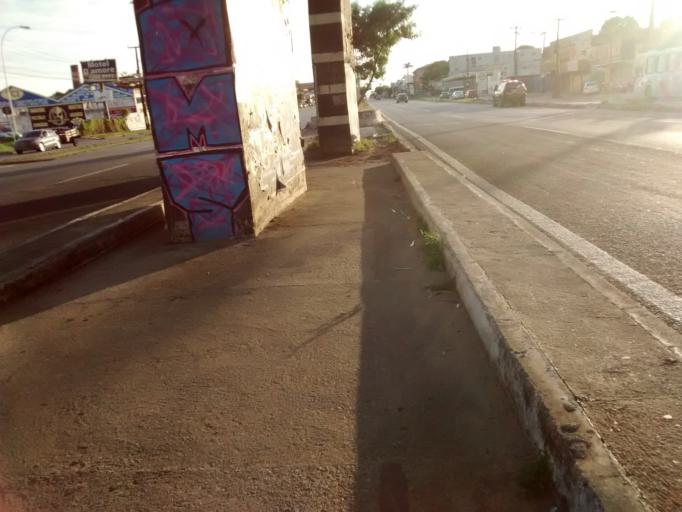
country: BR
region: Ceara
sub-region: Fortaleza
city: Fortaleza
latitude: -3.7388
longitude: -38.5852
